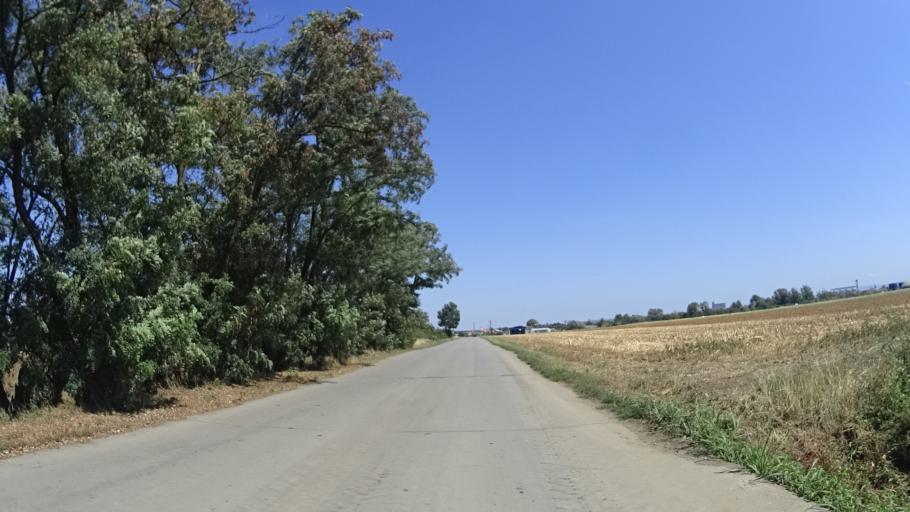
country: CZ
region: South Moravian
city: Petrov
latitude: 48.8886
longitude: 17.2936
